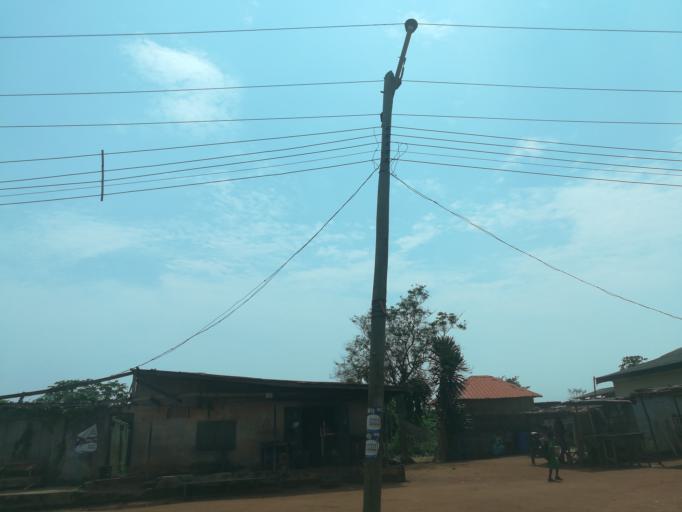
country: NG
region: Lagos
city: Ikorodu
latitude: 6.5759
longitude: 3.6291
